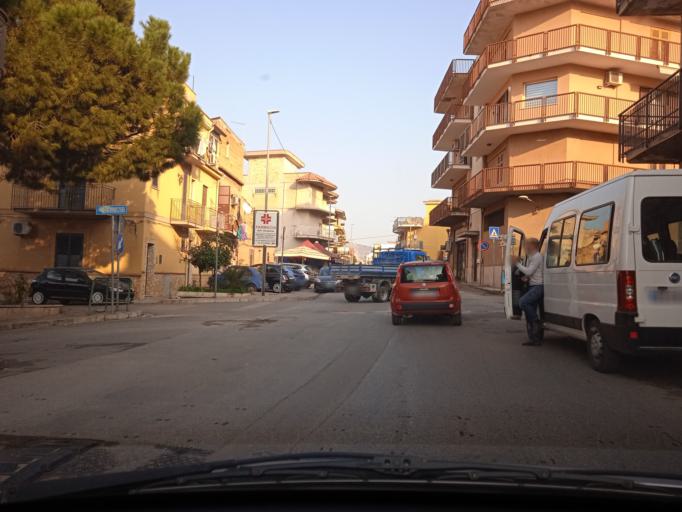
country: IT
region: Sicily
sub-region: Palermo
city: Villabate
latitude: 38.0757
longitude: 13.4413
